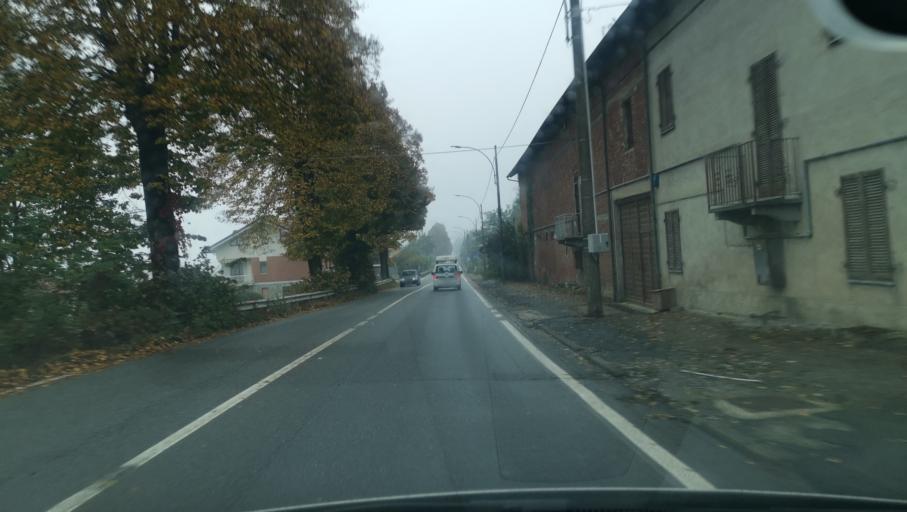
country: IT
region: Piedmont
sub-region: Provincia di Torino
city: Castiglione Torinese
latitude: 45.1177
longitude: 7.7871
